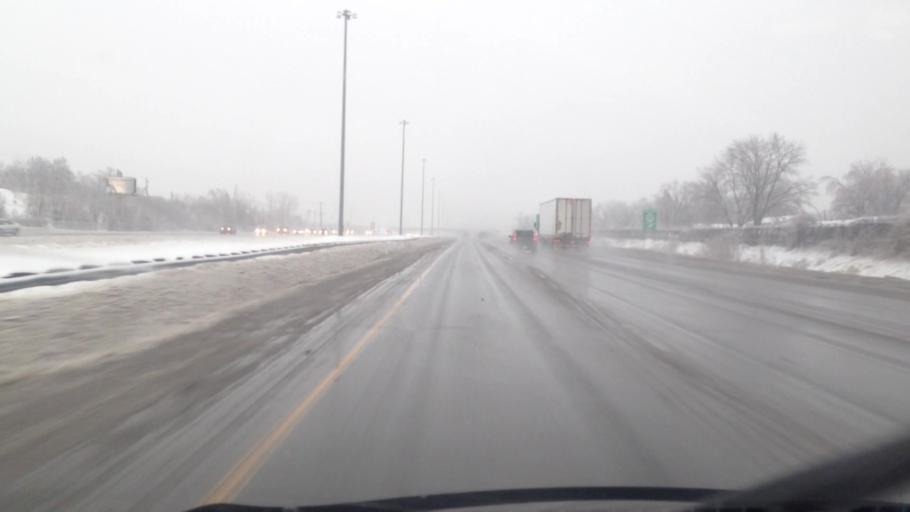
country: CA
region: Quebec
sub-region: Laurentides
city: Rosemere
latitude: 45.5894
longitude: -73.7963
